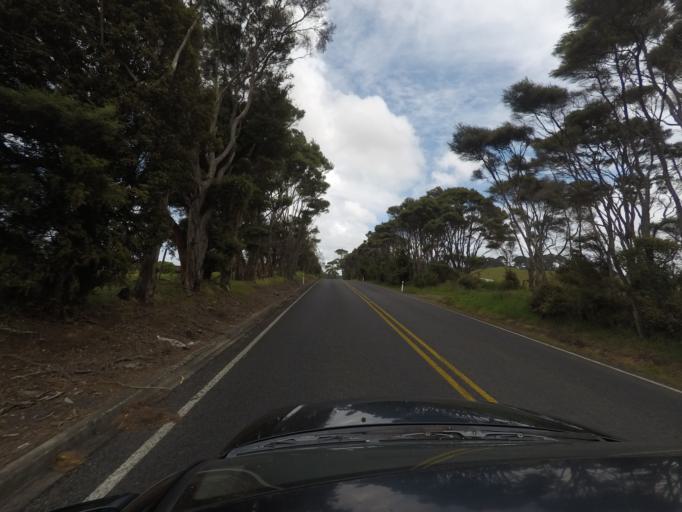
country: NZ
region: Auckland
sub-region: Auckland
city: Parakai
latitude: -36.6506
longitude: 174.5206
